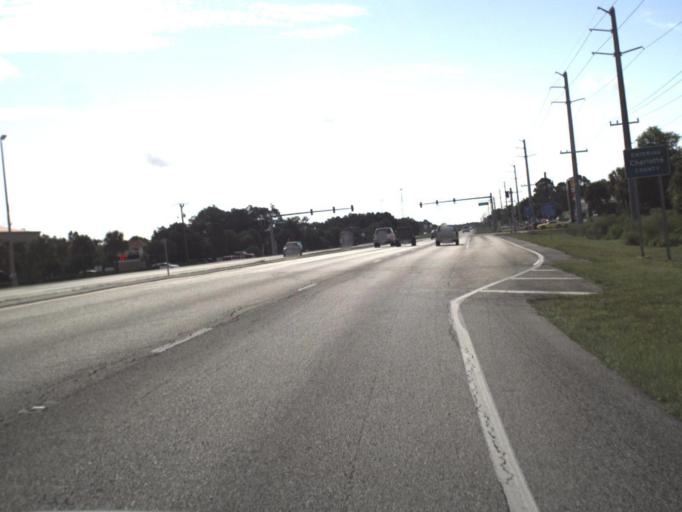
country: US
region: Florida
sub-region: Sarasota County
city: North Port
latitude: 27.0331
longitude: -82.2054
